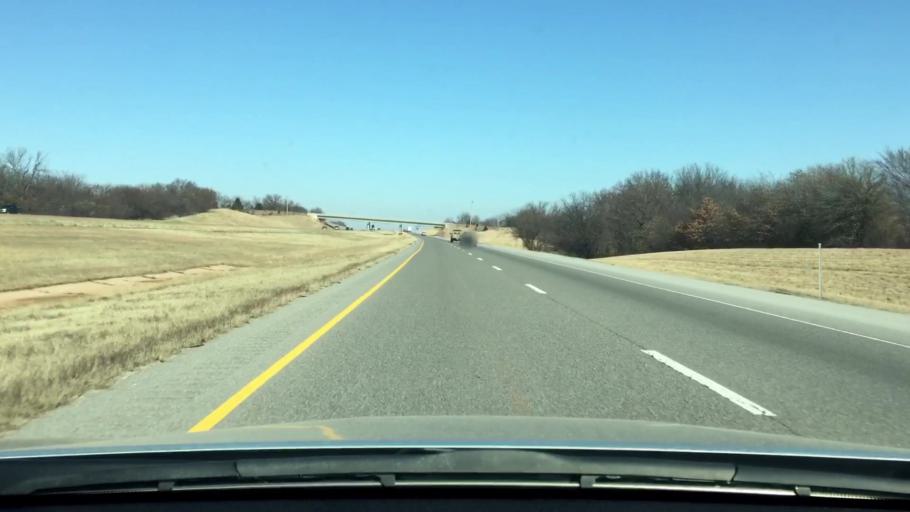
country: US
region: Oklahoma
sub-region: McClain County
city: Purcell
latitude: 34.9528
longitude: -97.3685
